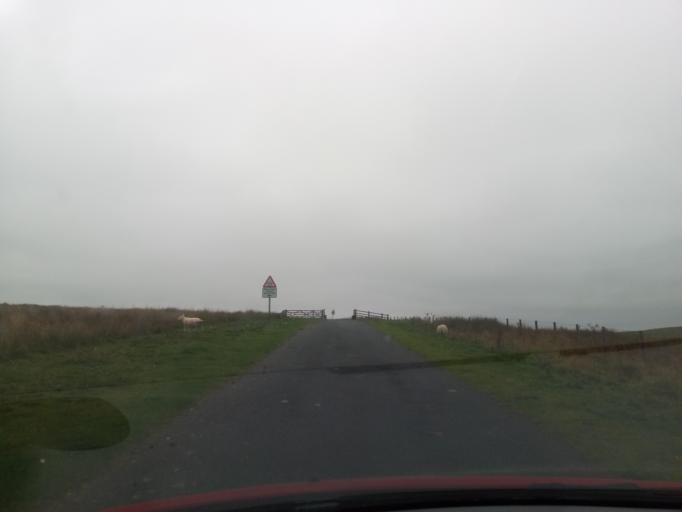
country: GB
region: England
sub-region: Northumberland
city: Rochester
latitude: 55.3059
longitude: -2.1943
